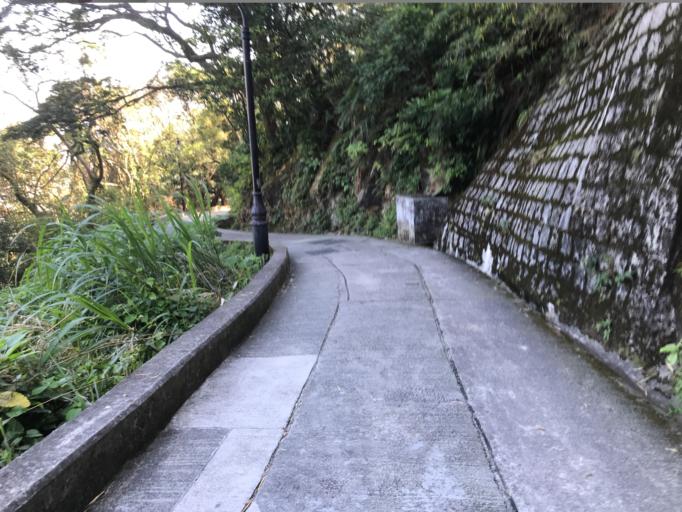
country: HK
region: Central and Western
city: Central
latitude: 22.2715
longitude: 114.1500
